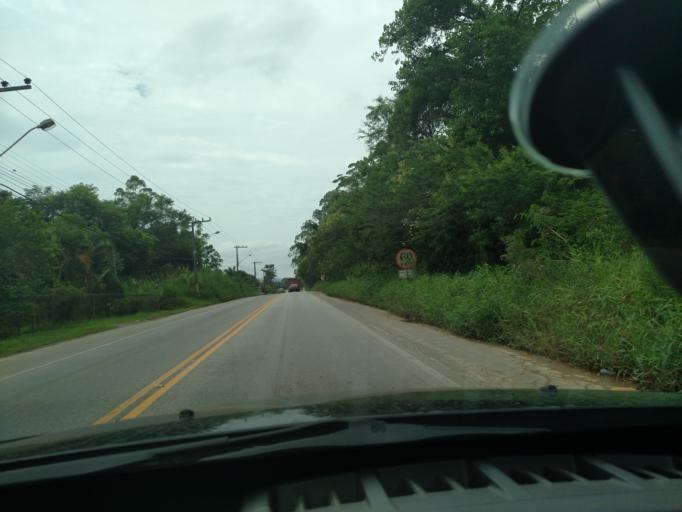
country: BR
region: Santa Catarina
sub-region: Itajai
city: Itajai
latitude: -26.8915
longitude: -48.7602
